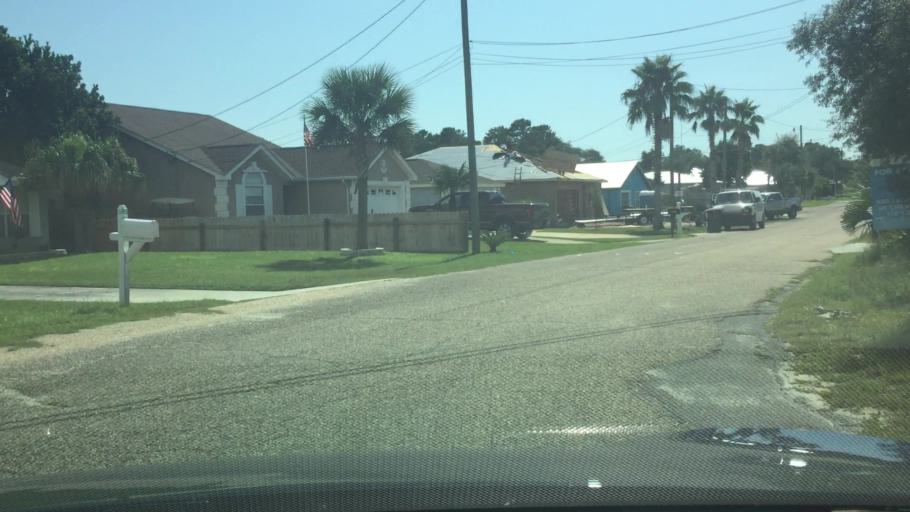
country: US
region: Florida
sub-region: Bay County
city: Laguna Beach
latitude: 30.2588
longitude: -85.9513
